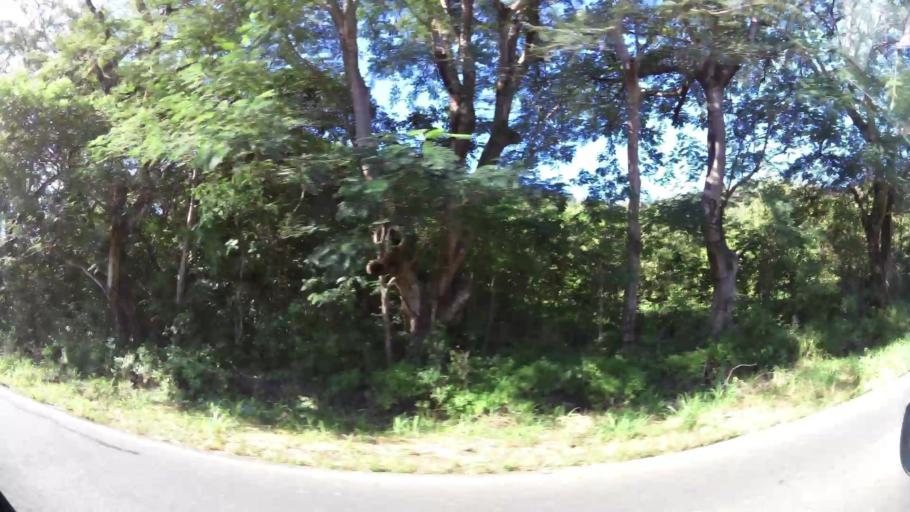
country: CR
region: Guanacaste
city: Belen
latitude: 10.3569
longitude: -85.7482
